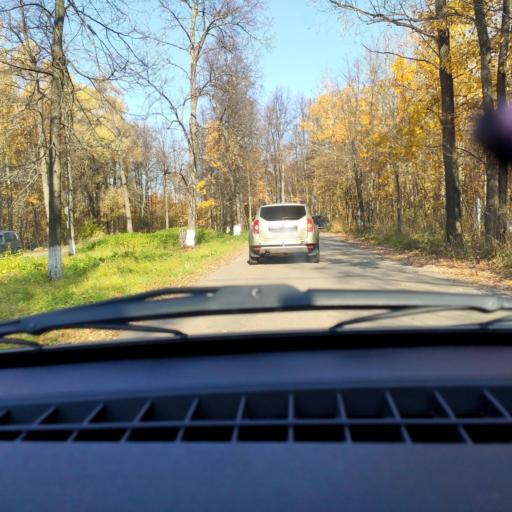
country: RU
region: Bashkortostan
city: Mikhaylovka
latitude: 54.8114
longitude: 55.8632
